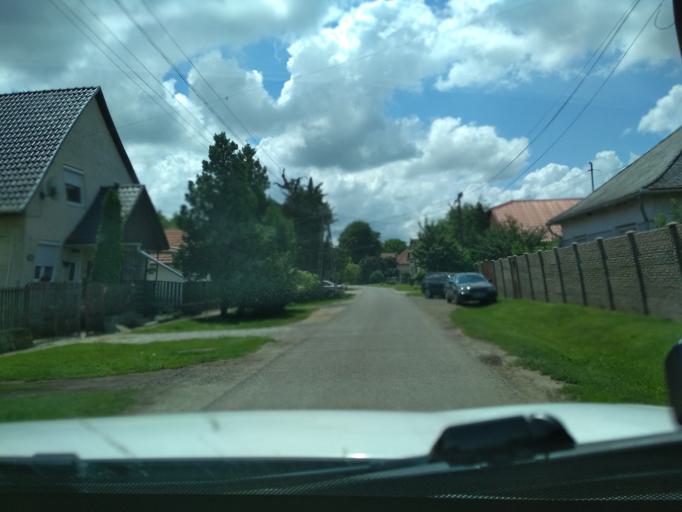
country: HU
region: Jasz-Nagykun-Szolnok
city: Tiszafured
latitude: 47.6104
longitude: 20.7780
